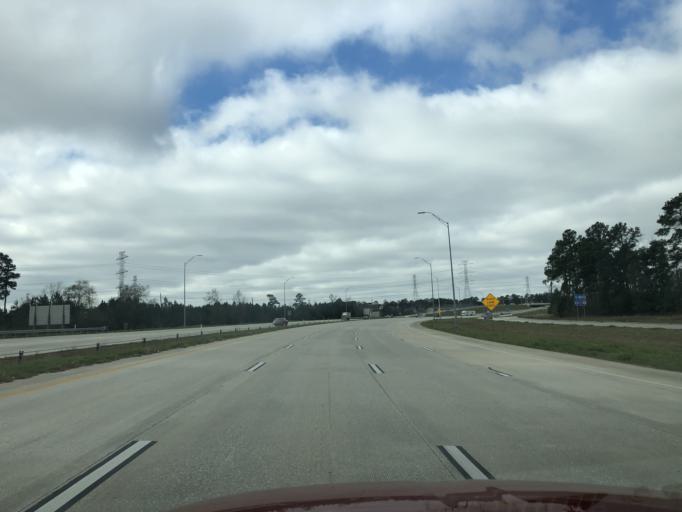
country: US
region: Texas
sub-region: Harris County
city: Spring
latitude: 30.0894
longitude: -95.4445
